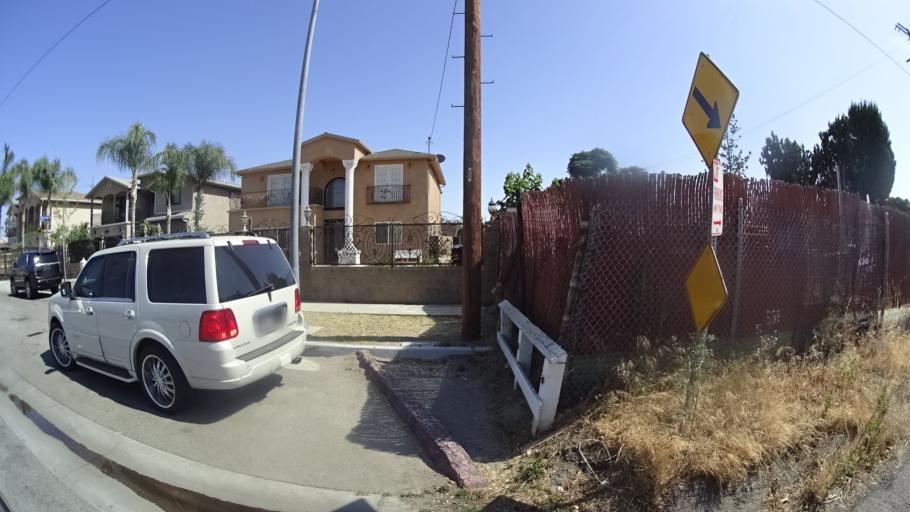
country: US
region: California
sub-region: Los Angeles County
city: Van Nuys
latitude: 34.2168
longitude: -118.4157
